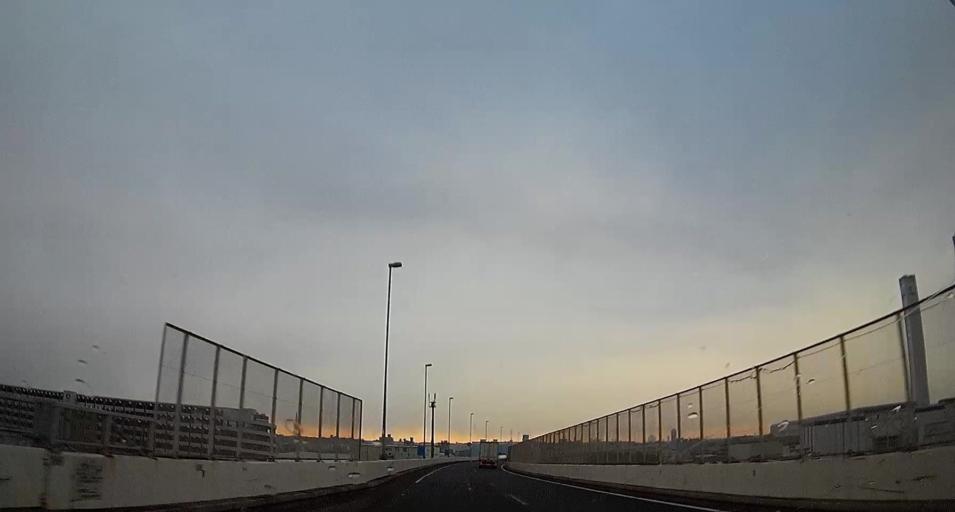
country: JP
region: Kanagawa
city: Yokohama
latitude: 35.4715
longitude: 139.6759
